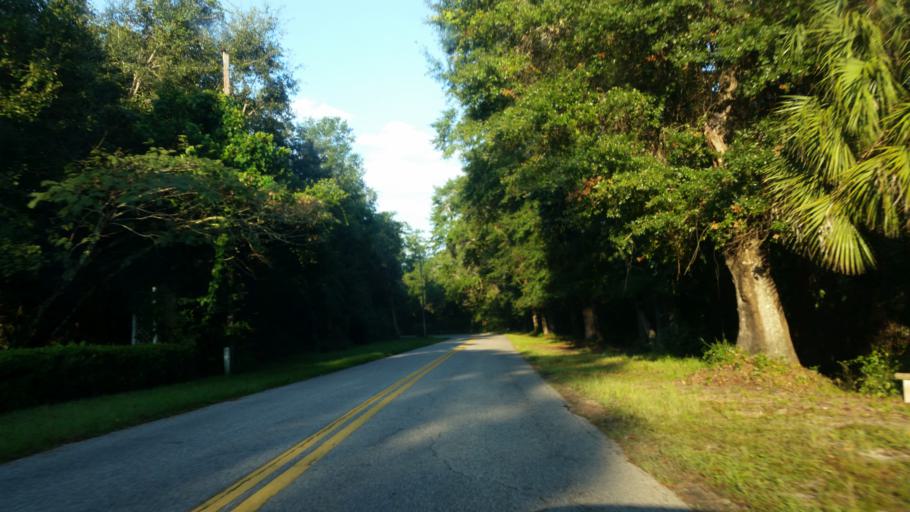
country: US
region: Florida
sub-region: Santa Rosa County
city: Milton
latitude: 30.6301
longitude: -87.0253
